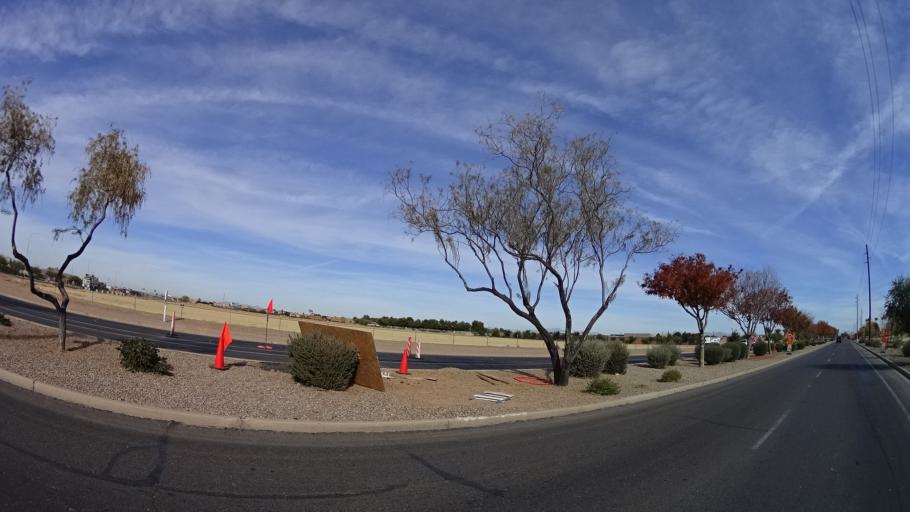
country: US
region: Arizona
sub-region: Maricopa County
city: Chandler
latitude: 33.2767
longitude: -111.8325
